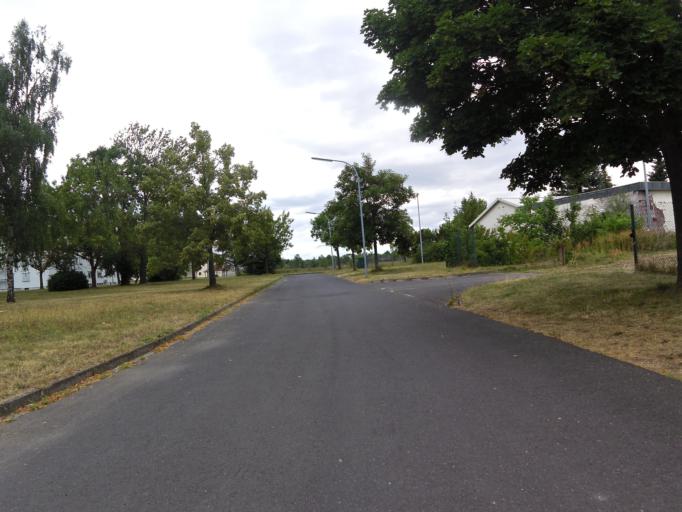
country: DE
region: Bavaria
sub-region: Regierungsbezirk Unterfranken
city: Gerbrunn
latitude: 49.7843
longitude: 9.9780
